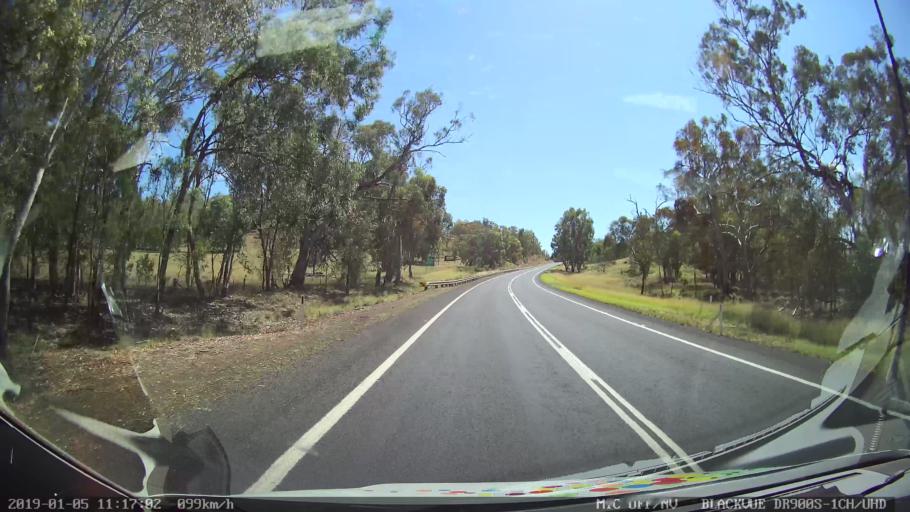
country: AU
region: New South Wales
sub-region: Warrumbungle Shire
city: Coonabarabran
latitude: -31.3308
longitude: 149.3027
